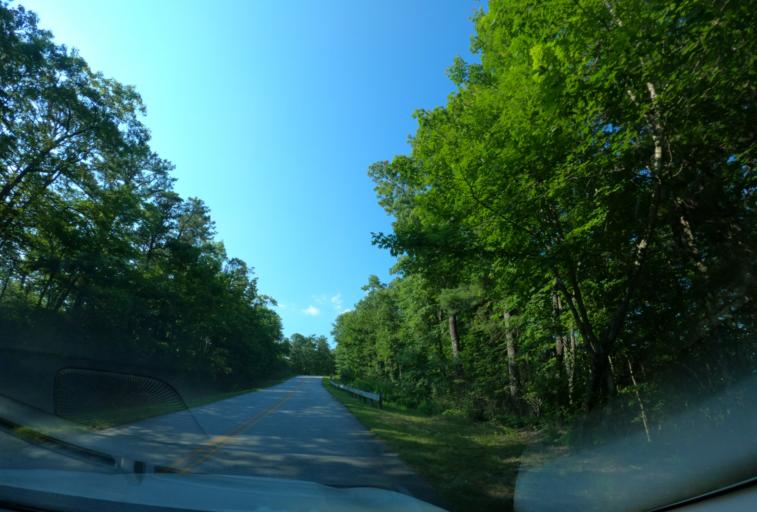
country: US
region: North Carolina
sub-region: Transylvania County
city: Brevard
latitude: 35.0910
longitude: -82.9510
